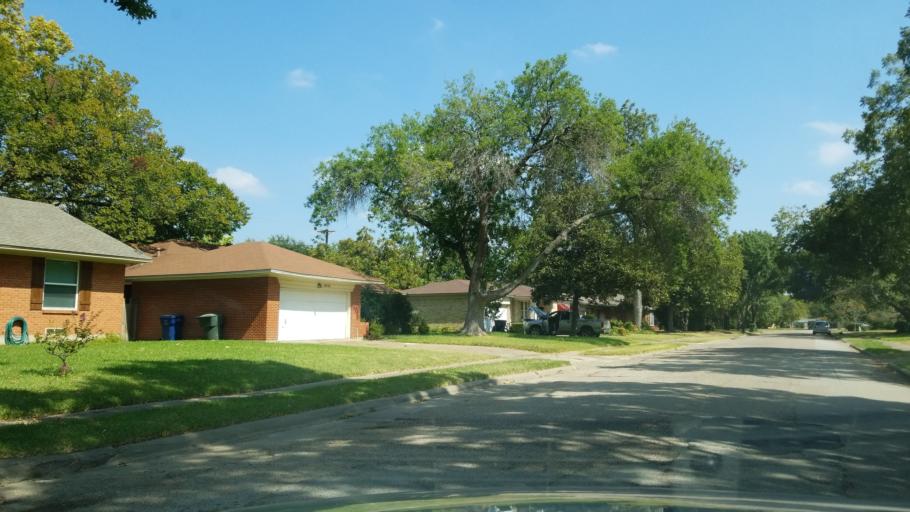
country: US
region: Texas
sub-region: Dallas County
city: Garland
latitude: 32.8987
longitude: -96.6617
